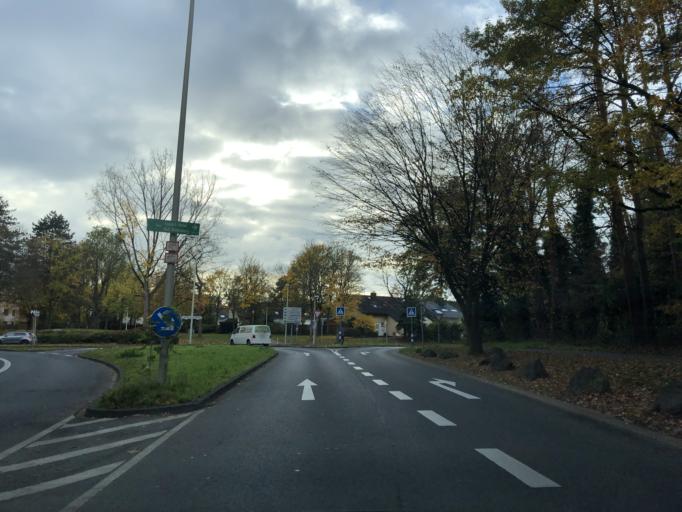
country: DE
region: North Rhine-Westphalia
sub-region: Regierungsbezirk Koln
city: Konigswinter
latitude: 50.6670
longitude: 7.1522
